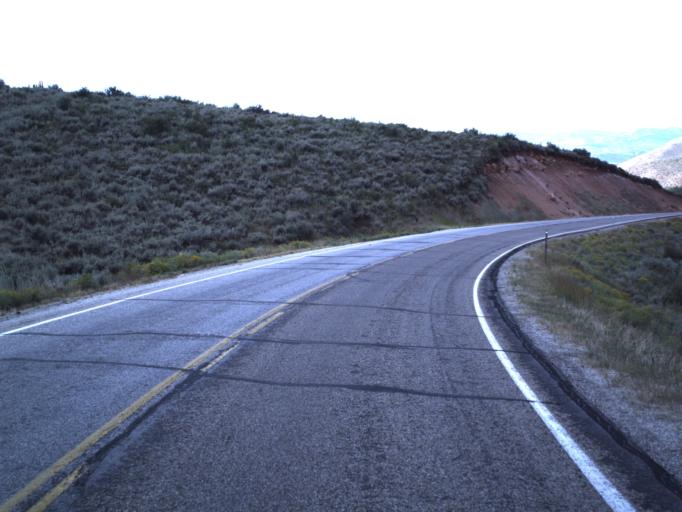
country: US
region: Utah
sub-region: Rich County
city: Randolph
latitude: 41.8084
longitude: -111.2592
